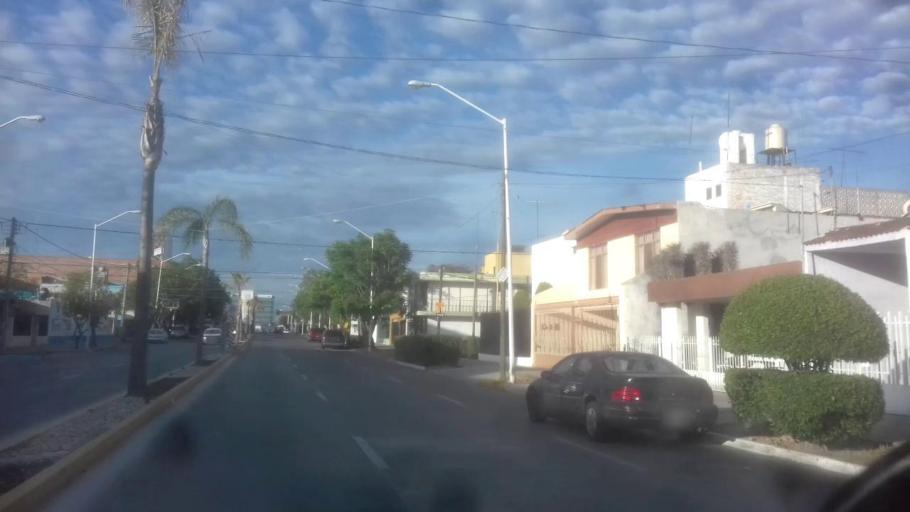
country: MX
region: Aguascalientes
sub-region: Aguascalientes
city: Aguascalientes
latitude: 21.8679
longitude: -102.2979
